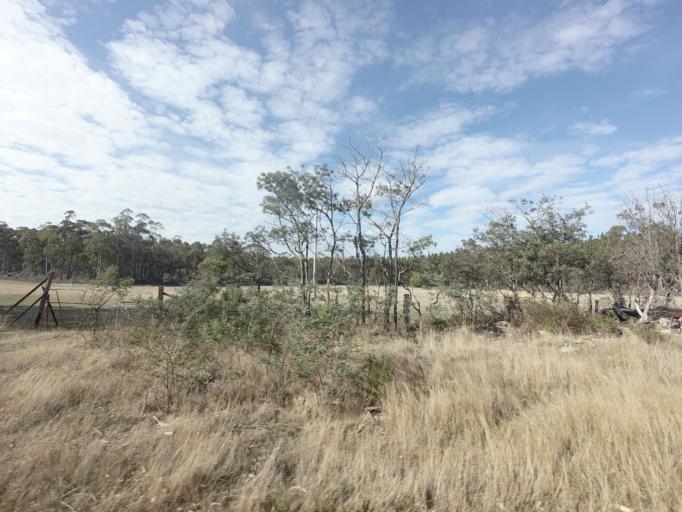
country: AU
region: Tasmania
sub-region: Sorell
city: Sorell
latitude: -42.5084
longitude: 147.4774
